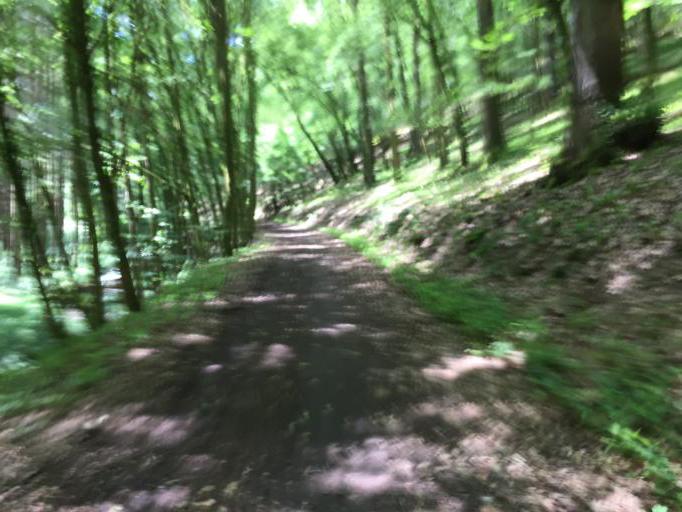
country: DE
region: Rheinland-Pfalz
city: Heilberscheid
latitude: 50.4327
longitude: 7.8761
